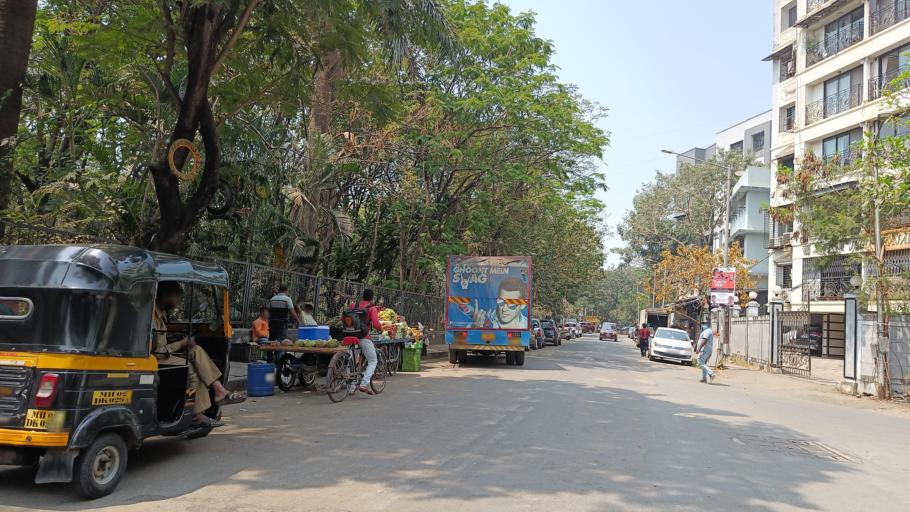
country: IN
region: Maharashtra
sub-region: Mumbai Suburban
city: Mumbai
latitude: 19.1124
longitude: 72.8309
